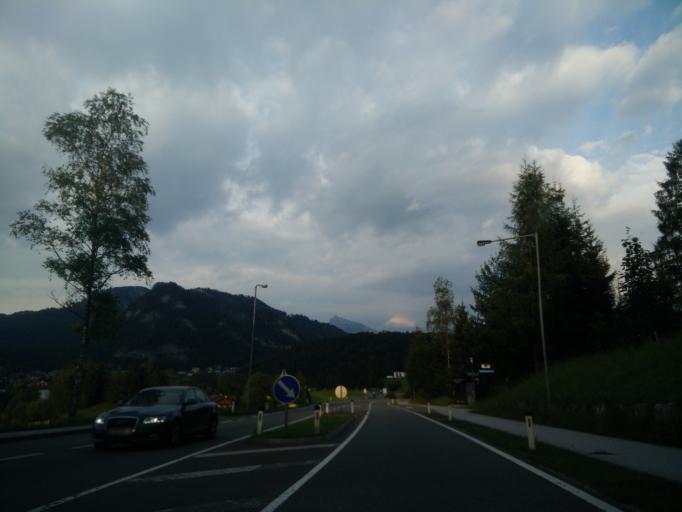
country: AT
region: Salzburg
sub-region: Politischer Bezirk Salzburg-Umgebung
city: Fuschl am See
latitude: 47.7926
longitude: 13.2851
